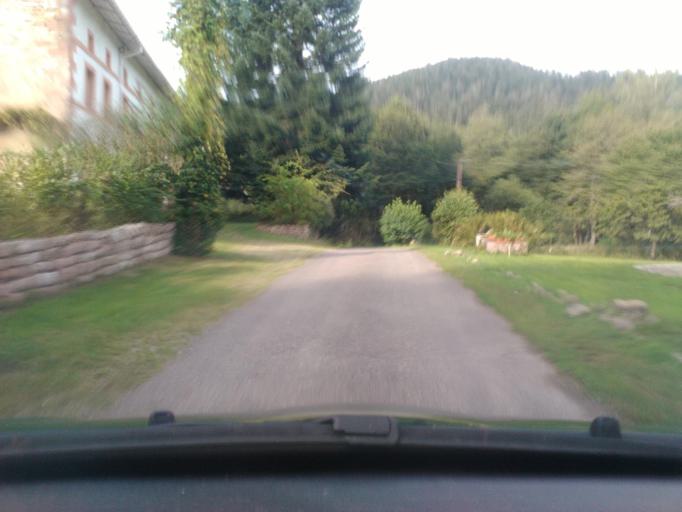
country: FR
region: Lorraine
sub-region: Departement des Vosges
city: Taintrux
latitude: 48.2426
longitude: 6.8460
